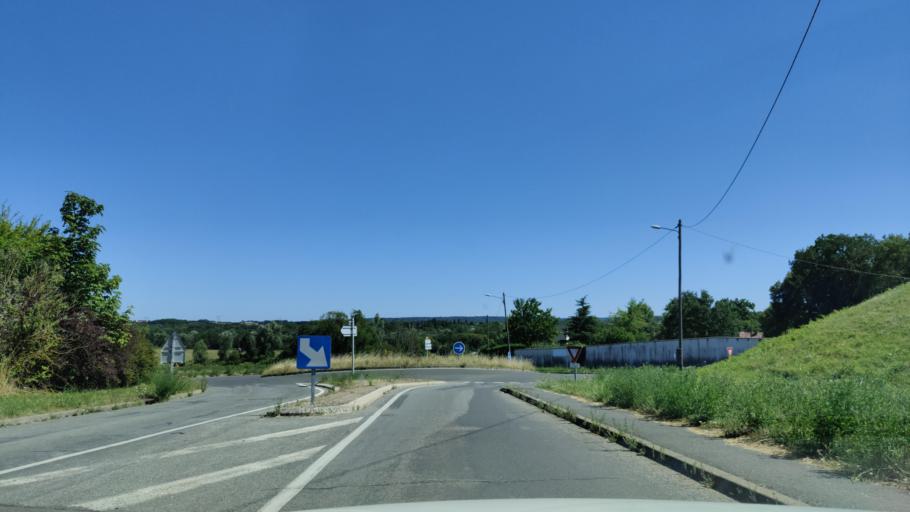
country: FR
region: Ile-de-France
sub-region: Departement de l'Essonne
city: Bruyeres-le-Chatel
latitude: 48.5868
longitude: 2.1906
